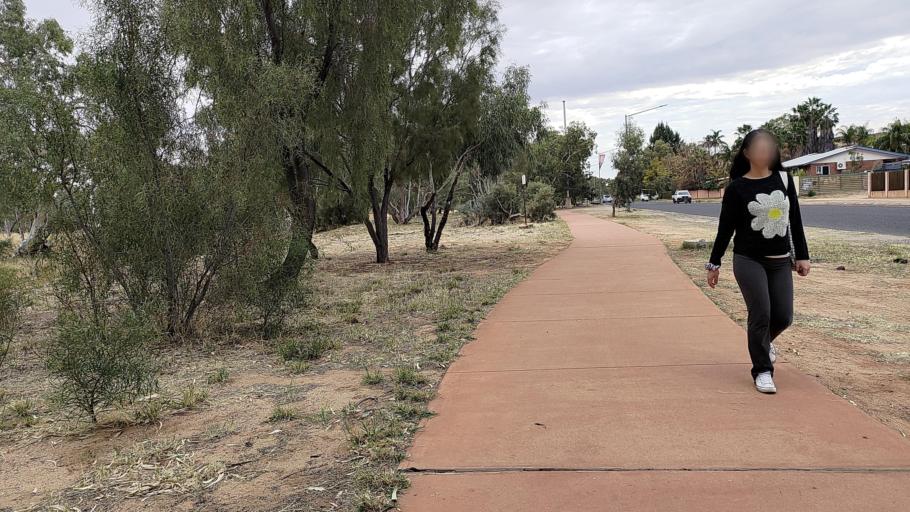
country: AU
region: Northern Territory
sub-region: Alice Springs
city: Alice Springs
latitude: -23.7106
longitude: 133.8805
